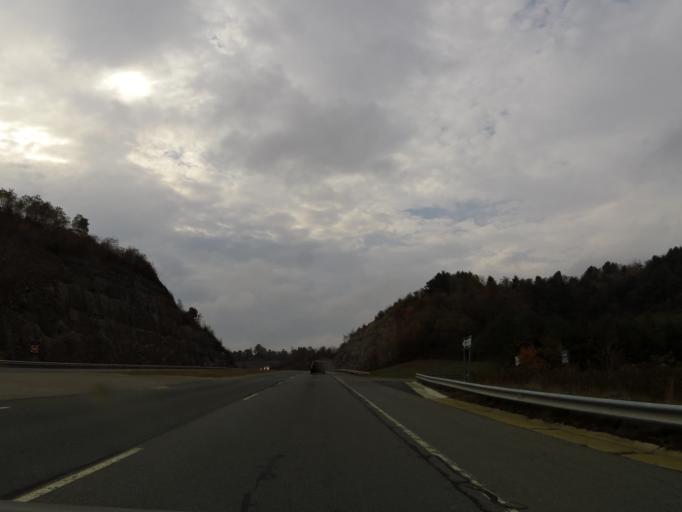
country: US
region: North Carolina
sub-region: Watauga County
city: Boone
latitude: 36.2301
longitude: -81.5871
